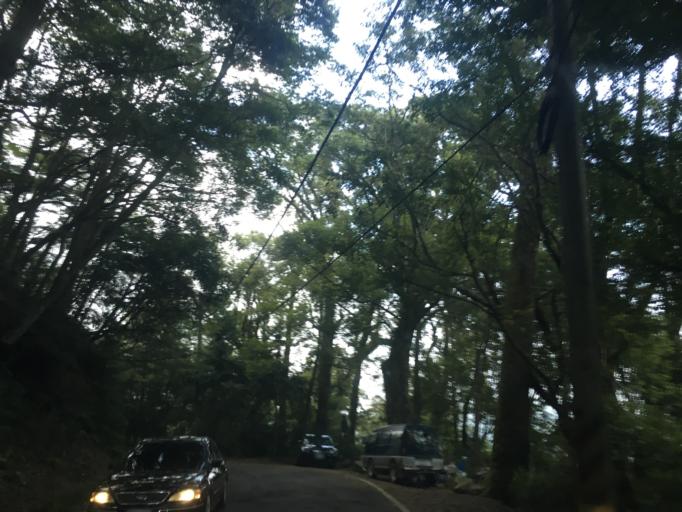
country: TW
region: Taiwan
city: Fengyuan
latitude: 24.2347
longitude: 120.9812
